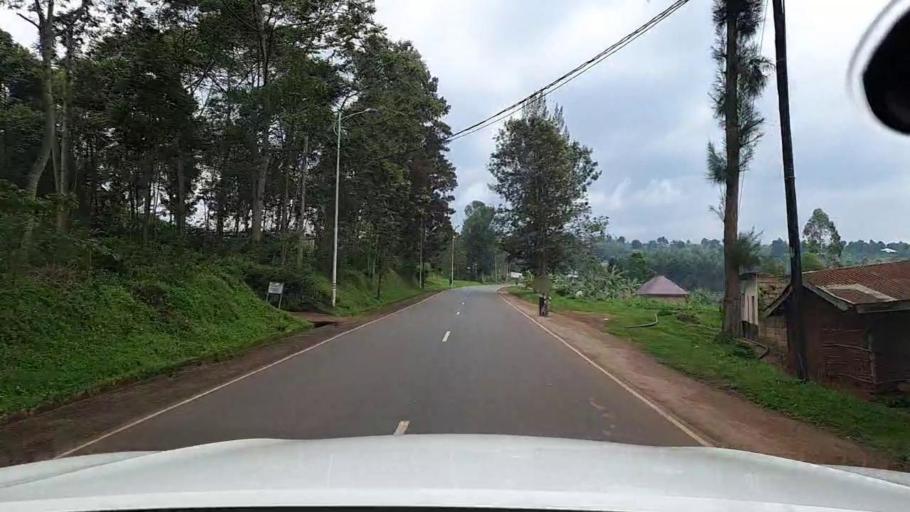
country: RW
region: Western Province
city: Cyangugu
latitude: -2.5370
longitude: 28.8931
